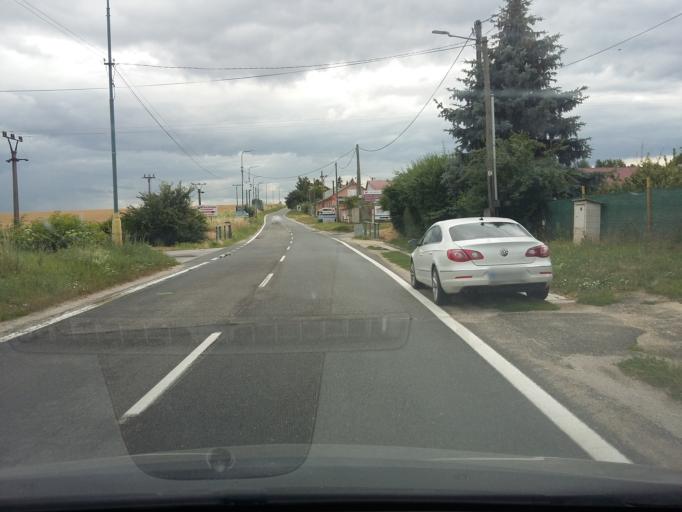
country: SK
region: Trnavsky
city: Vrbove
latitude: 48.6139
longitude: 17.7183
